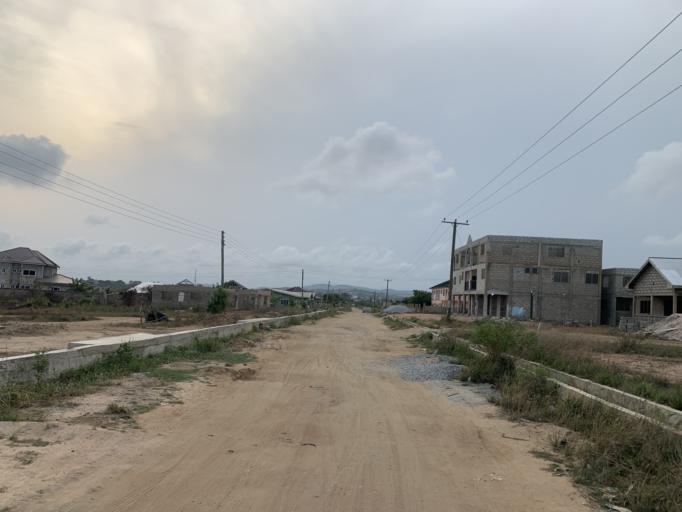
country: GH
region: Central
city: Winneba
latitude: 5.3831
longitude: -0.6283
